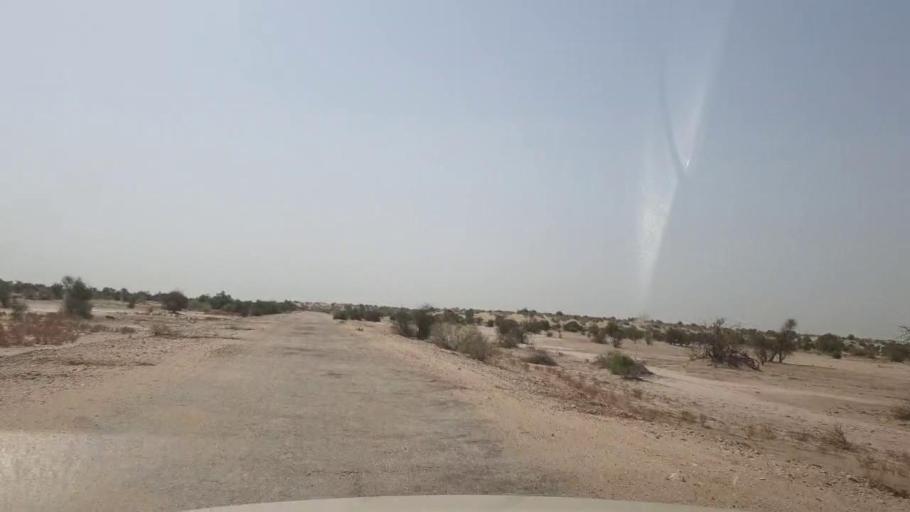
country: PK
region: Sindh
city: Rohri
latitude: 27.4397
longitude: 69.2428
